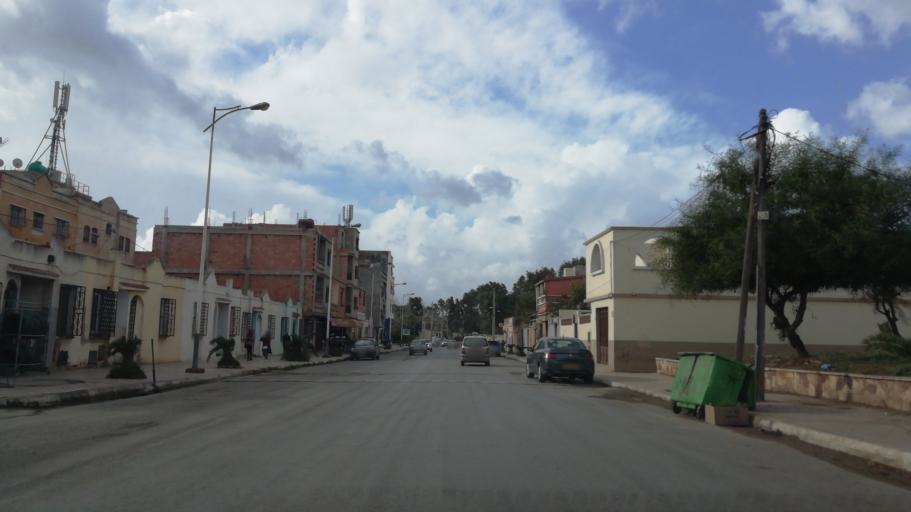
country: DZ
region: Oran
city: Oran
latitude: 35.6789
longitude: -0.6195
